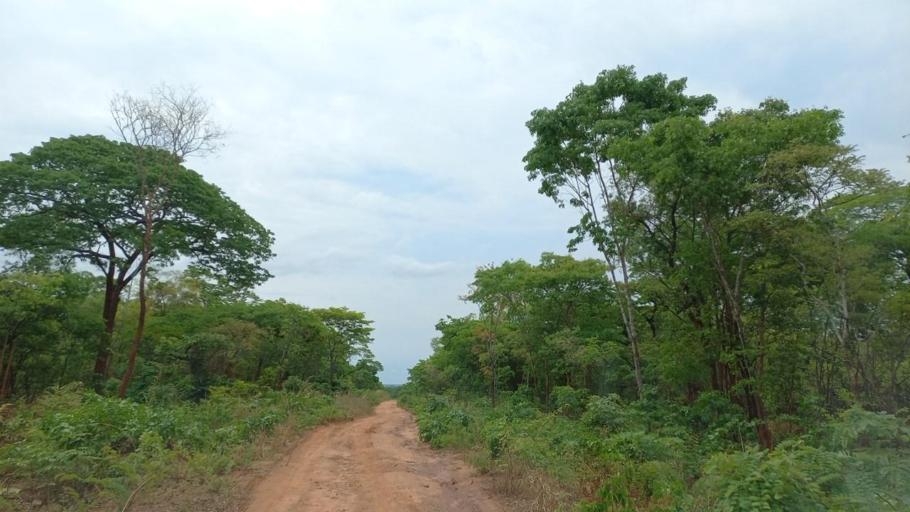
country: ZM
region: North-Western
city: Kalengwa
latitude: -13.6221
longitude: 24.9769
